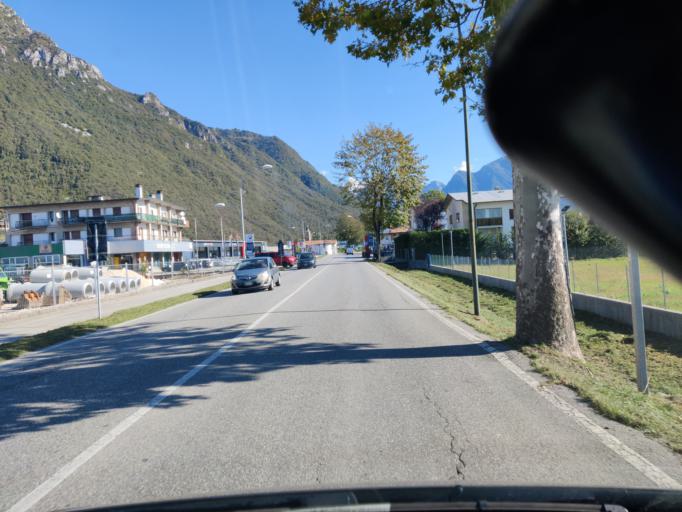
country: IT
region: Veneto
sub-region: Provincia di Belluno
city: Belluno
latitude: 46.1657
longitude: 12.2446
